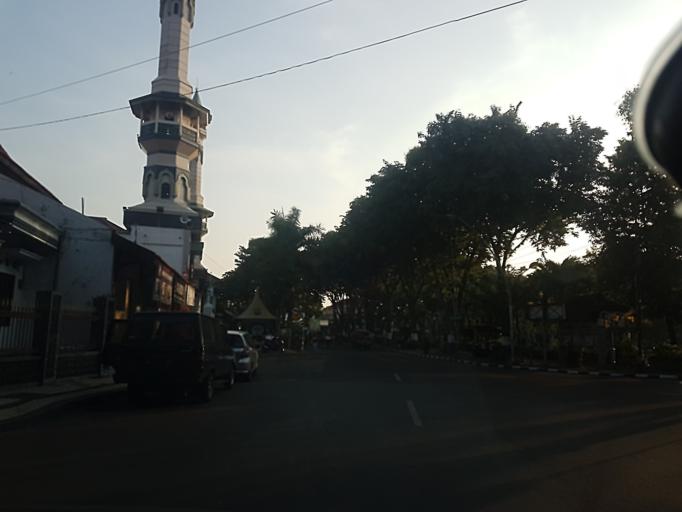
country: ID
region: East Java
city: Gresik
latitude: -7.1576
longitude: 112.6552
